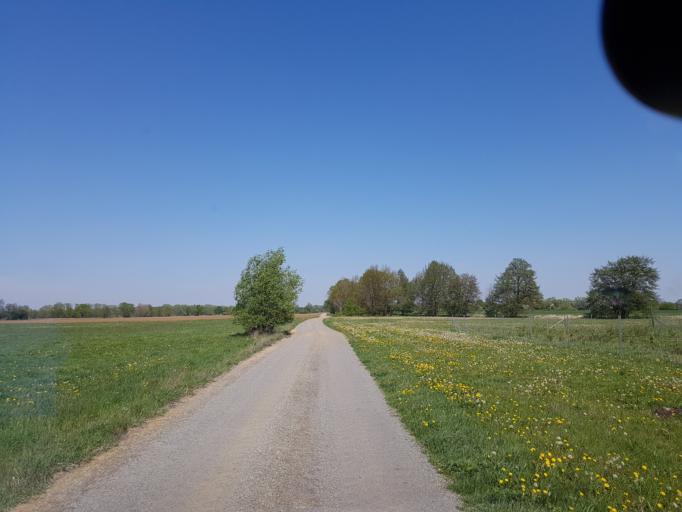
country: DE
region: Brandenburg
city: Schonewalde
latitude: 51.6758
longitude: 13.5820
